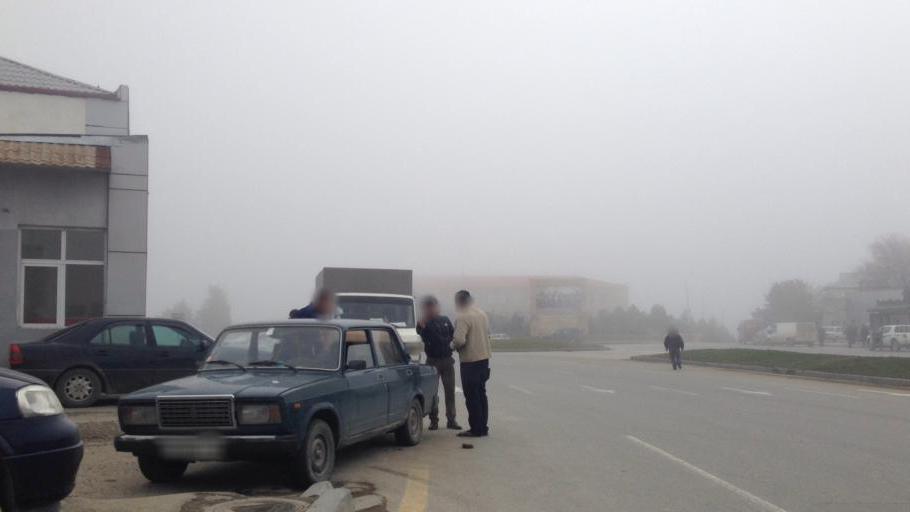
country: AZ
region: Baki
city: Qaracuxur
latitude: 40.3490
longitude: 49.9611
